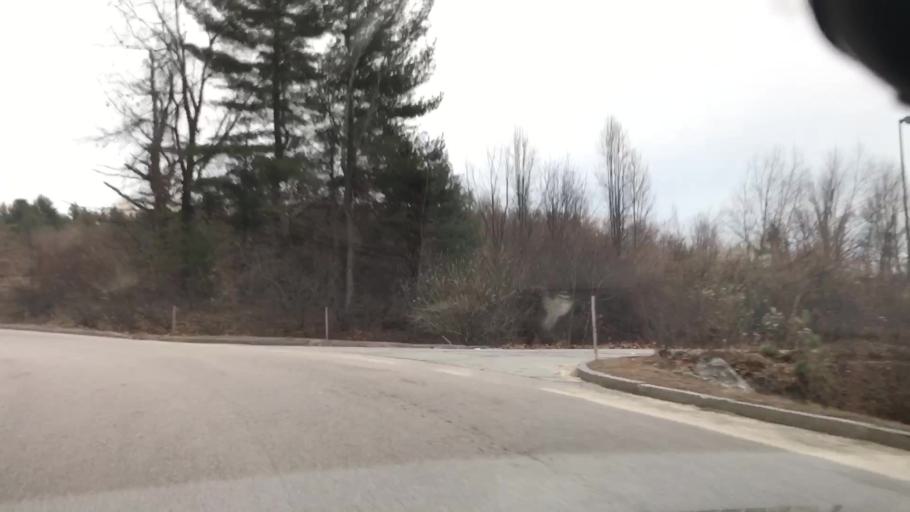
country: US
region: New Hampshire
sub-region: Hillsborough County
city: Hollis
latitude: 42.8051
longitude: -71.5496
